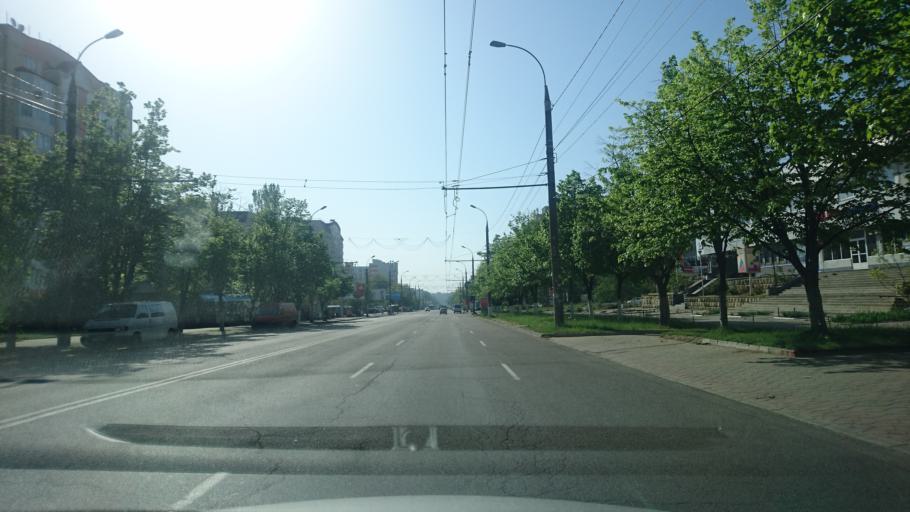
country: MD
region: Chisinau
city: Vatra
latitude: 47.0361
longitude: 28.7743
